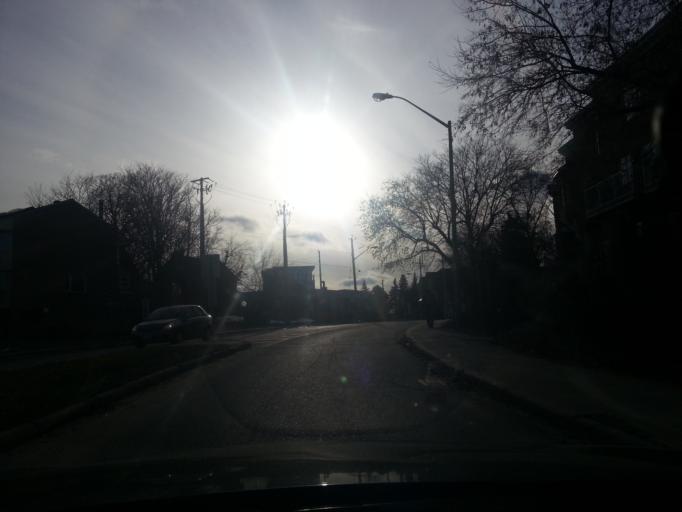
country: CA
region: Ontario
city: Ottawa
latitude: 45.4173
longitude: -75.6786
